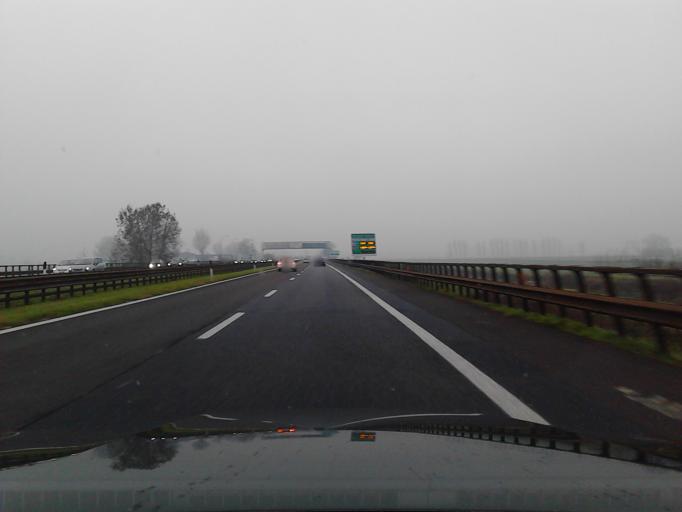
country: IT
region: Lombardy
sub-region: Provincia di Mantova
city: San Biagio
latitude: 45.0708
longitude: 10.8452
